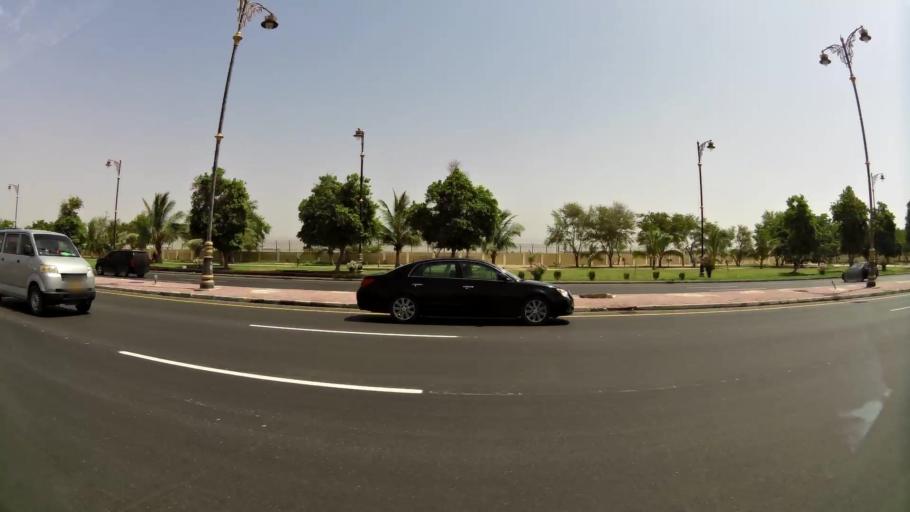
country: OM
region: Zufar
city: Salalah
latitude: 17.0230
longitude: 54.1034
